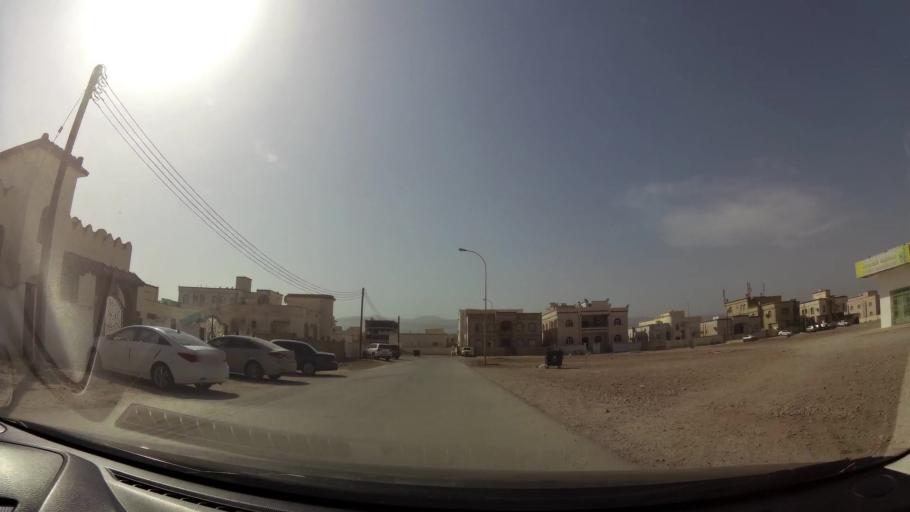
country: OM
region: Zufar
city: Salalah
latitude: 17.0056
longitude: 54.0084
